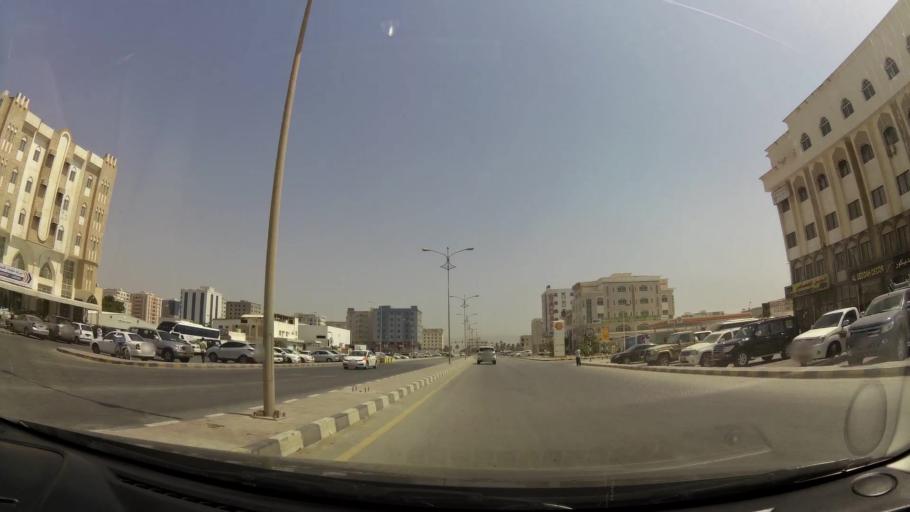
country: OM
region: Zufar
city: Salalah
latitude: 17.0179
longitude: 54.1009
